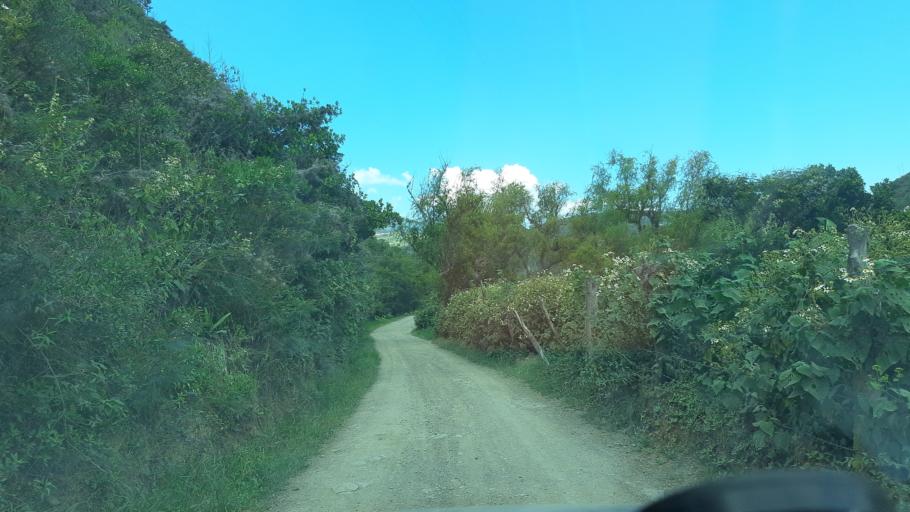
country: CO
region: Boyaca
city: Villa de Leiva
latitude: 5.6818
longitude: -73.5679
